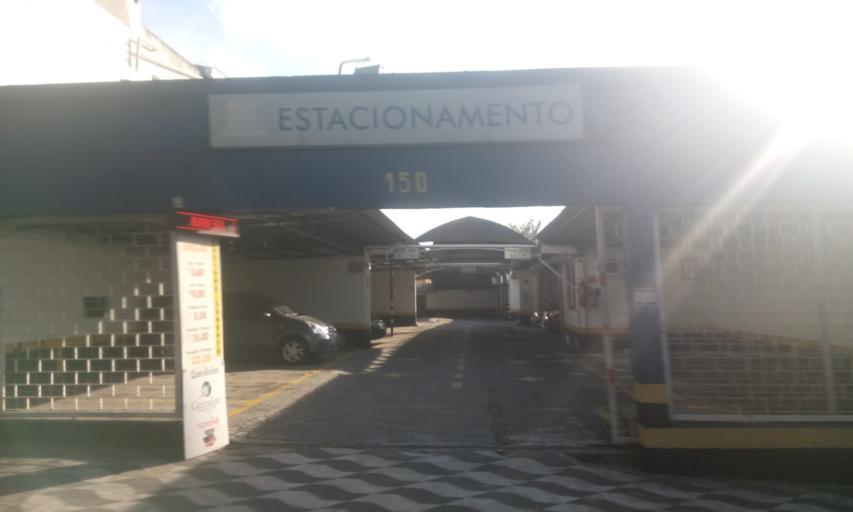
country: BR
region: Sao Paulo
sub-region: Sao Paulo
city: Sao Paulo
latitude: -23.5852
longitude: -46.6109
